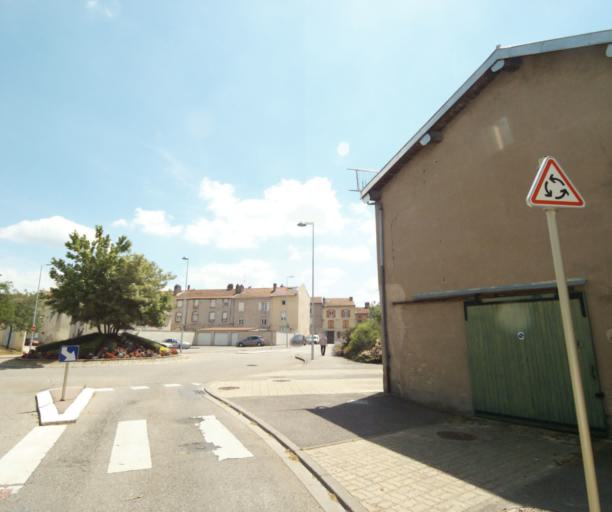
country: FR
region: Lorraine
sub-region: Departement de Meurthe-et-Moselle
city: Luneville
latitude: 48.5980
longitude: 6.4859
